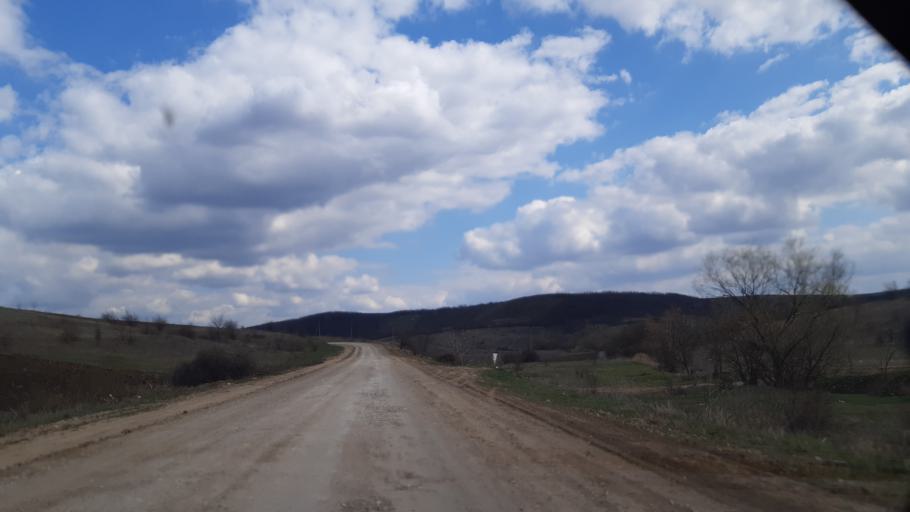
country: MD
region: Laloveni
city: Ialoveni
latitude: 46.8895
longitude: 28.7084
